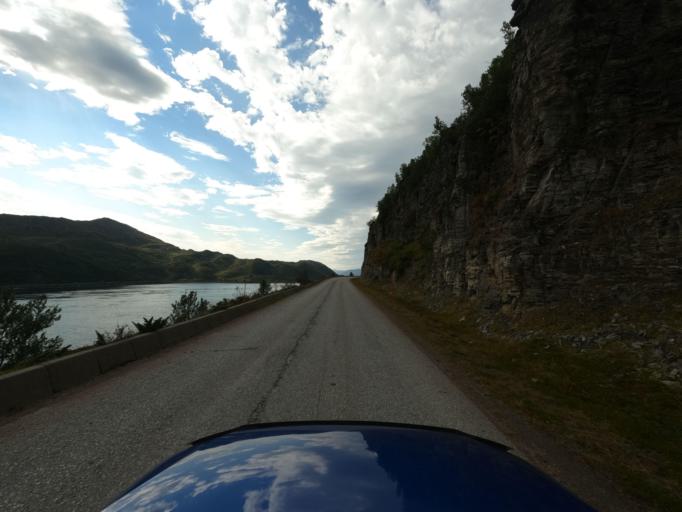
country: NO
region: Finnmark Fylke
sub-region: Kvalsund
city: Kvalsund
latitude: 70.5115
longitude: 23.9231
